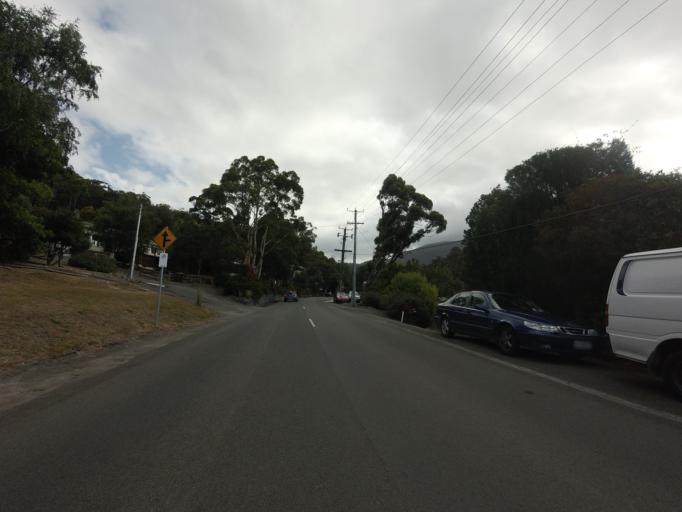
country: AU
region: Tasmania
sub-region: Hobart
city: Dynnyrne
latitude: -42.9011
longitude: 147.2813
